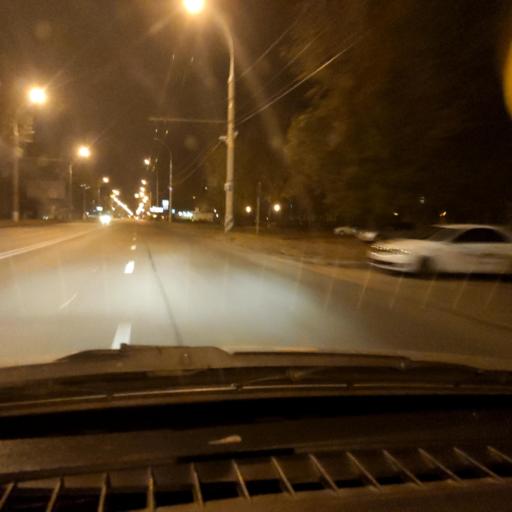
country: RU
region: Samara
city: Tol'yatti
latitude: 53.5063
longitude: 49.2803
